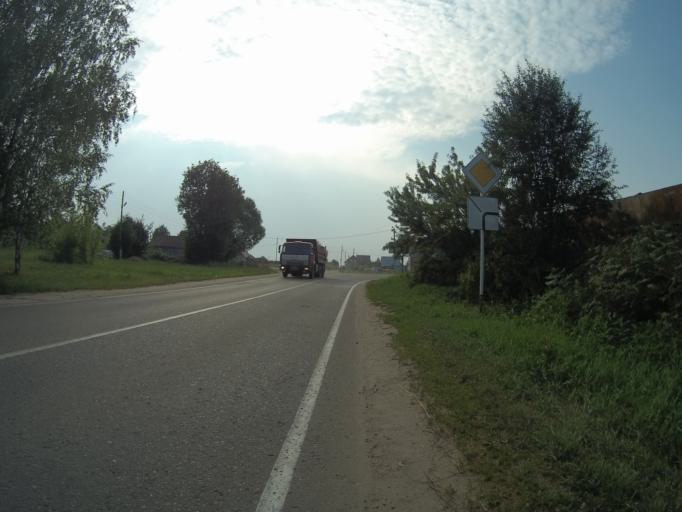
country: RU
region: Vladimir
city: Suzdal'
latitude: 56.4279
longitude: 40.4181
